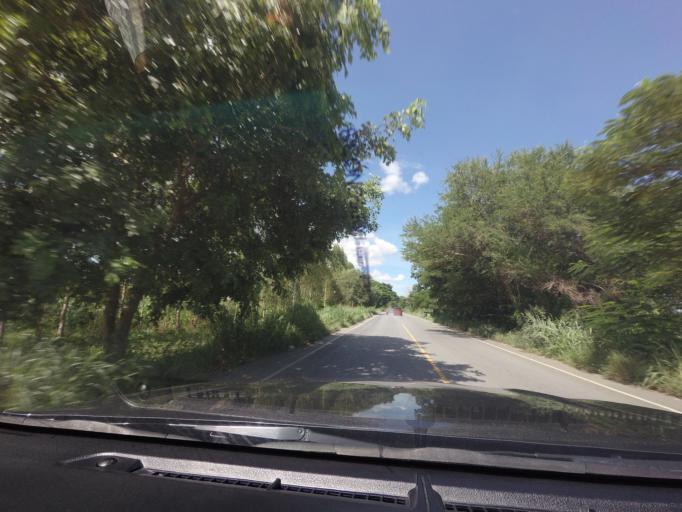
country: TH
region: Kanchanaburi
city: Phanom Thuan
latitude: 14.1746
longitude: 99.7816
